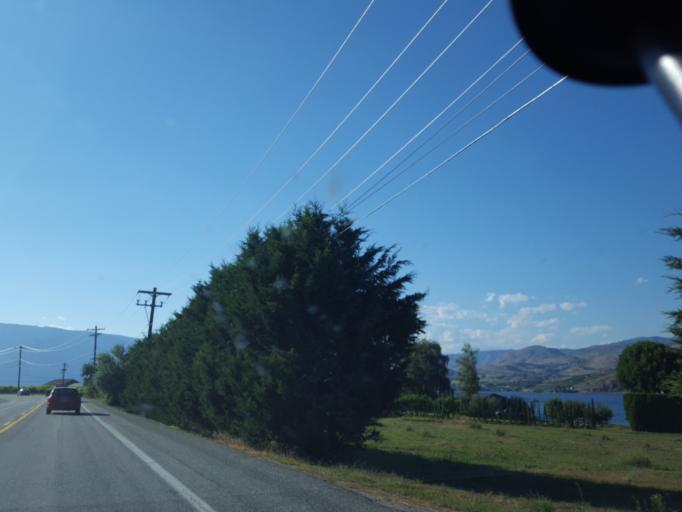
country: US
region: Washington
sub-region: Chelan County
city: Manson
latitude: 47.8422
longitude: -120.0949
